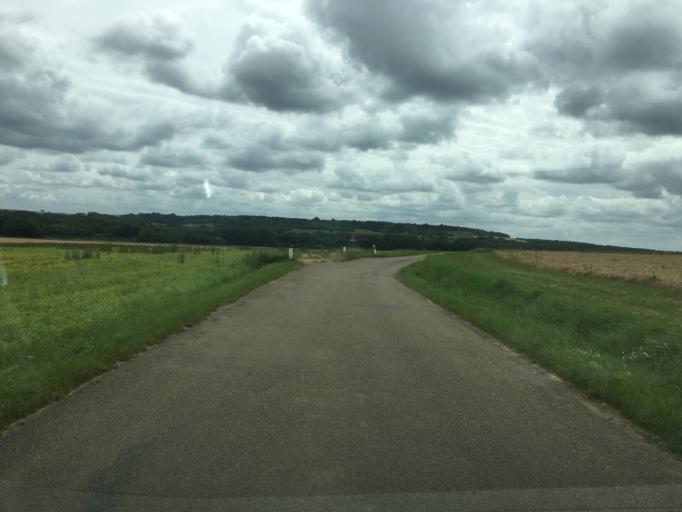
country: FR
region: Bourgogne
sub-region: Departement de l'Yonne
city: Fleury-la-Vallee
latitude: 47.8778
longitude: 3.4297
